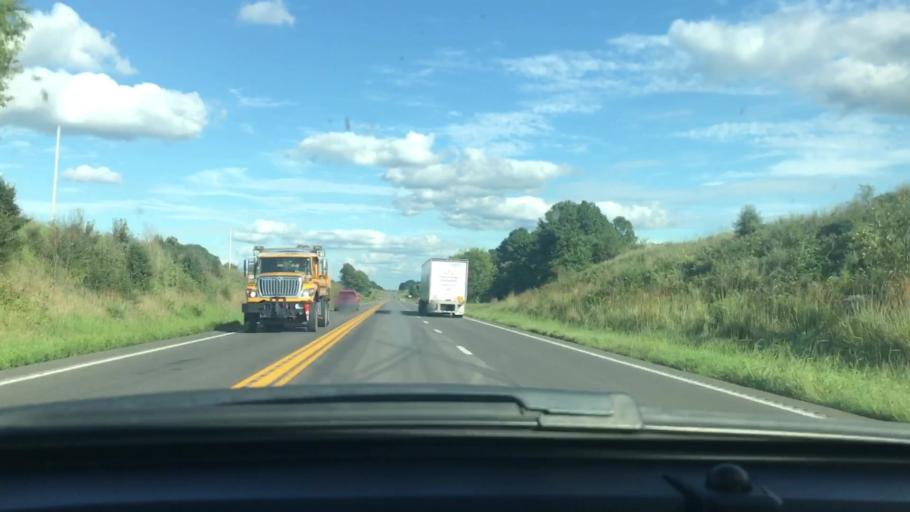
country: US
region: Missouri
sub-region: Oregon County
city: Thayer
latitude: 36.5875
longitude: -91.6323
